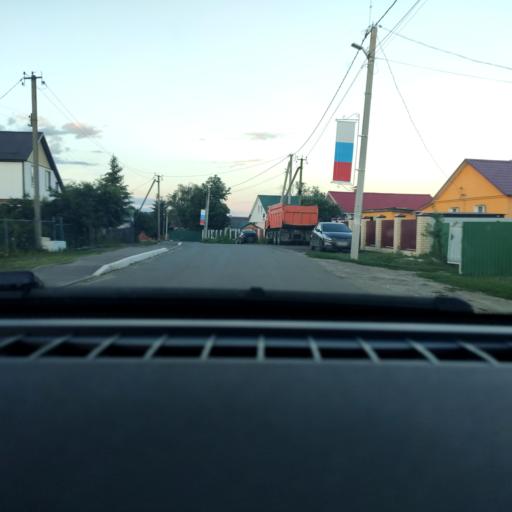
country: RU
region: Voronezj
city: Novaya Usman'
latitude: 51.6559
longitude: 39.3360
